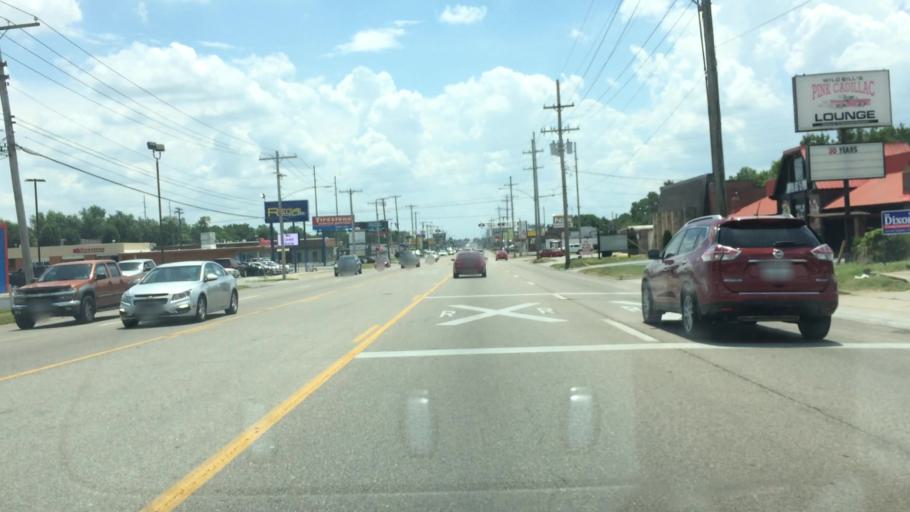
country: US
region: Missouri
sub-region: Greene County
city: Springfield
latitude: 37.2006
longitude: -93.2620
